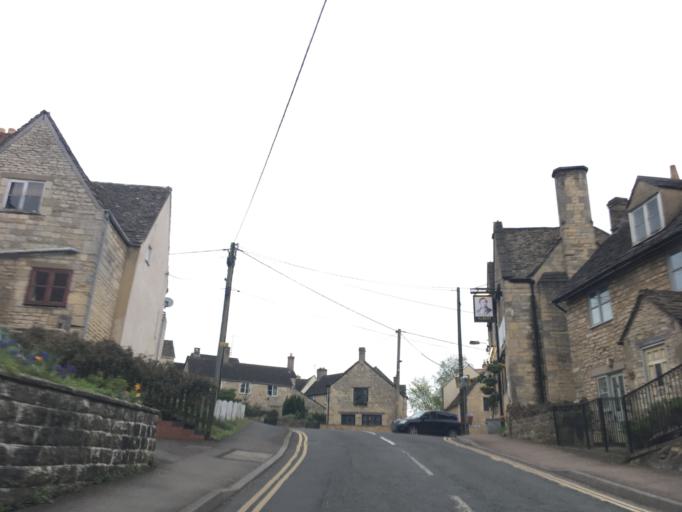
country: GB
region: England
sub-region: Gloucestershire
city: Stroud
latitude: 51.7392
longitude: -2.2249
